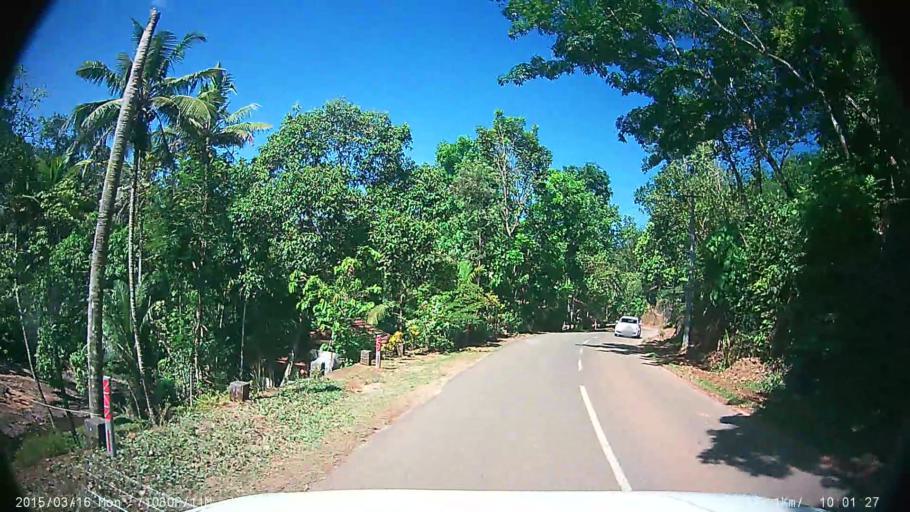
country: IN
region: Kerala
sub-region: Kottayam
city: Palackattumala
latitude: 9.7819
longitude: 76.5836
